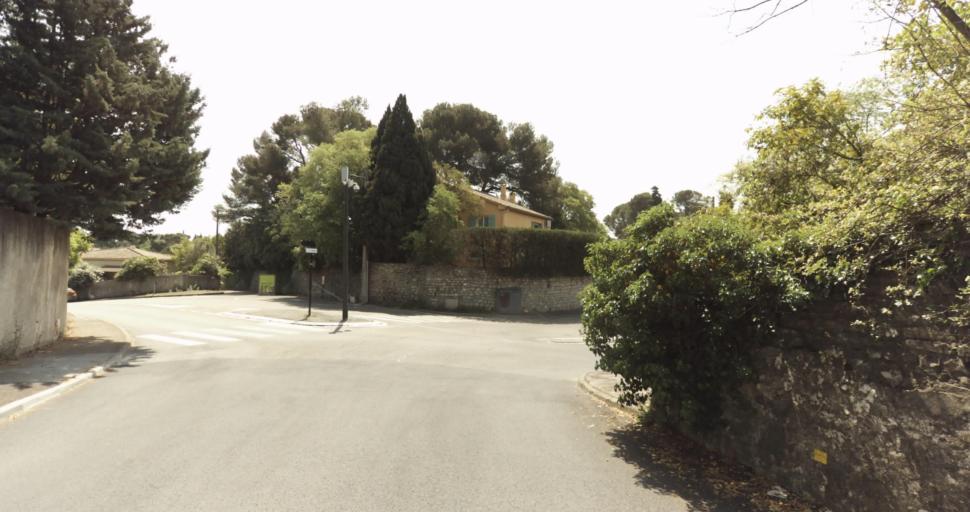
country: FR
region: Languedoc-Roussillon
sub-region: Departement du Gard
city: Nimes
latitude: 43.8489
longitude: 4.3497
